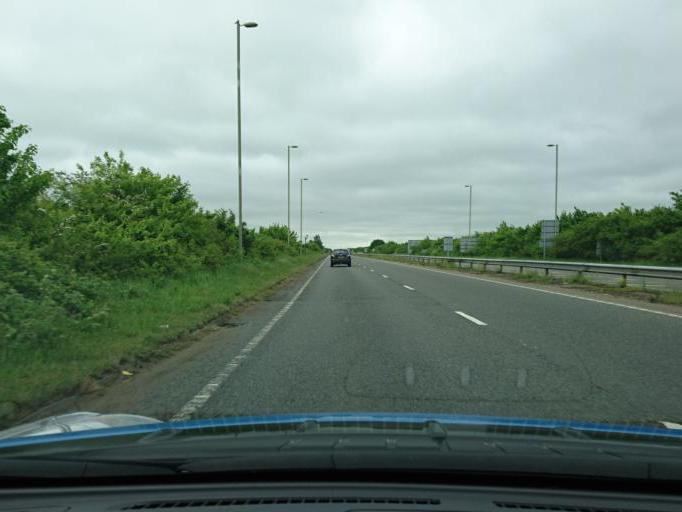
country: GB
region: England
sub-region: Oxfordshire
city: Frilford
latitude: 51.6852
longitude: -1.4111
